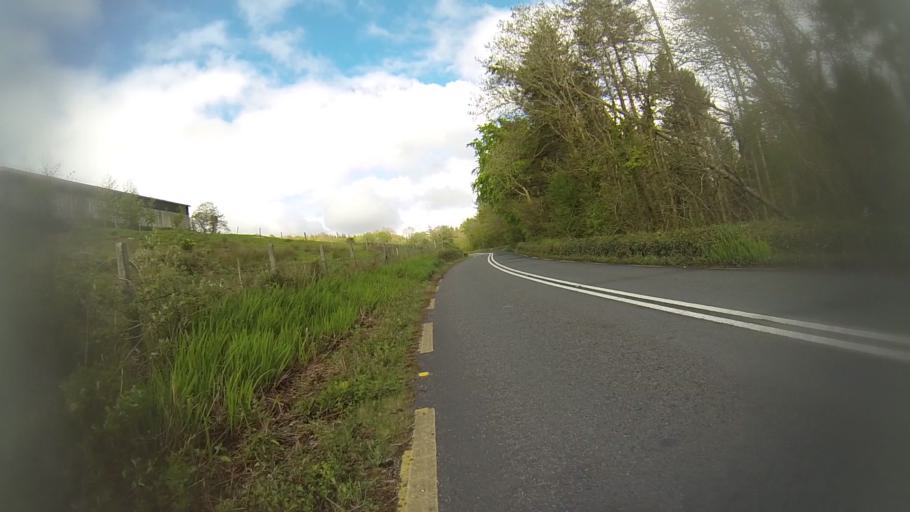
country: IE
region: Munster
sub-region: Ciarrai
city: Kenmare
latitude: 51.8565
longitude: -9.7293
